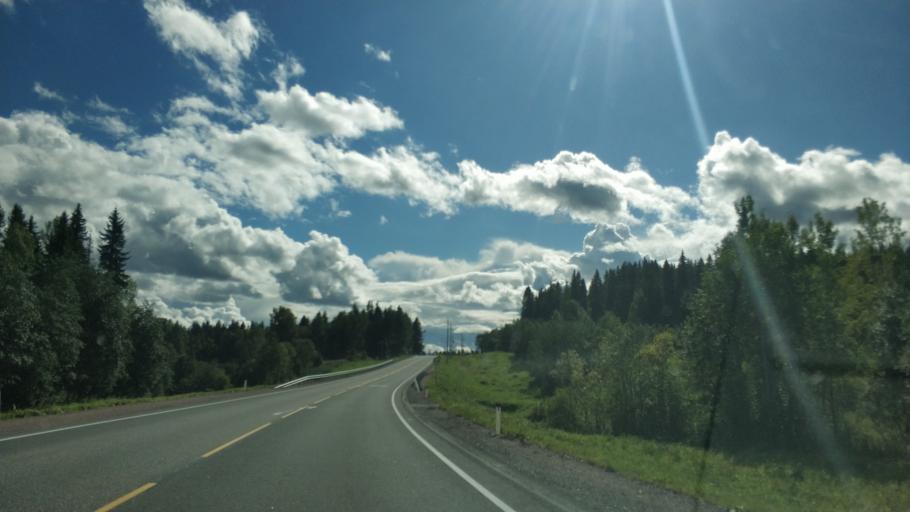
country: RU
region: Republic of Karelia
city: Ruskeala
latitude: 61.8874
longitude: 30.6444
